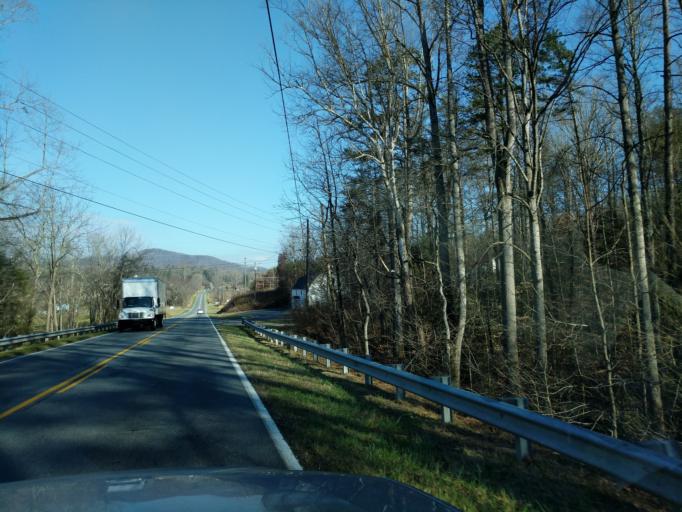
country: US
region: North Carolina
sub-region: McDowell County
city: West Marion
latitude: 35.6175
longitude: -81.9858
